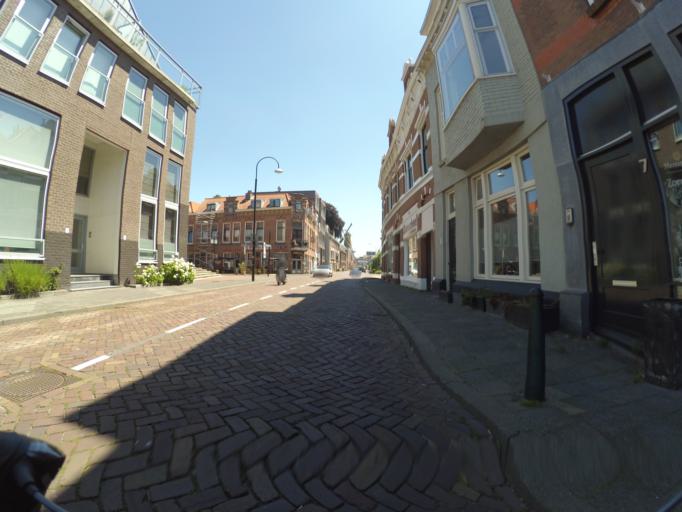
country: NL
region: South Holland
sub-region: Gemeente Dordrecht
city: Dordrecht
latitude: 51.8165
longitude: 4.6749
